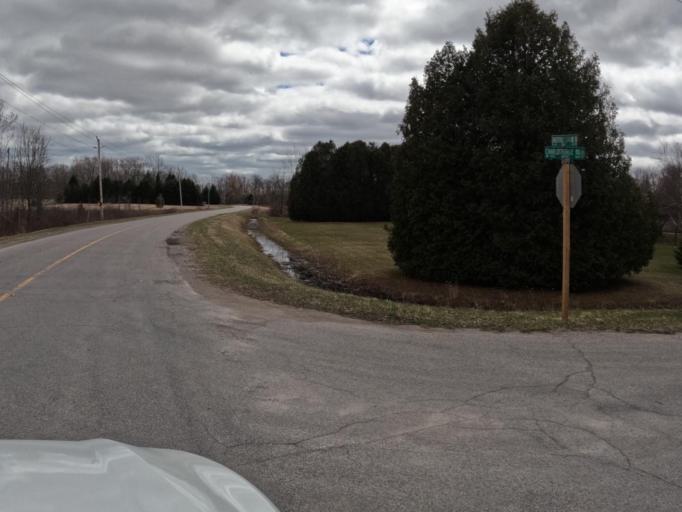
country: CA
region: Ontario
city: Norfolk County
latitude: 42.8022
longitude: -80.3660
